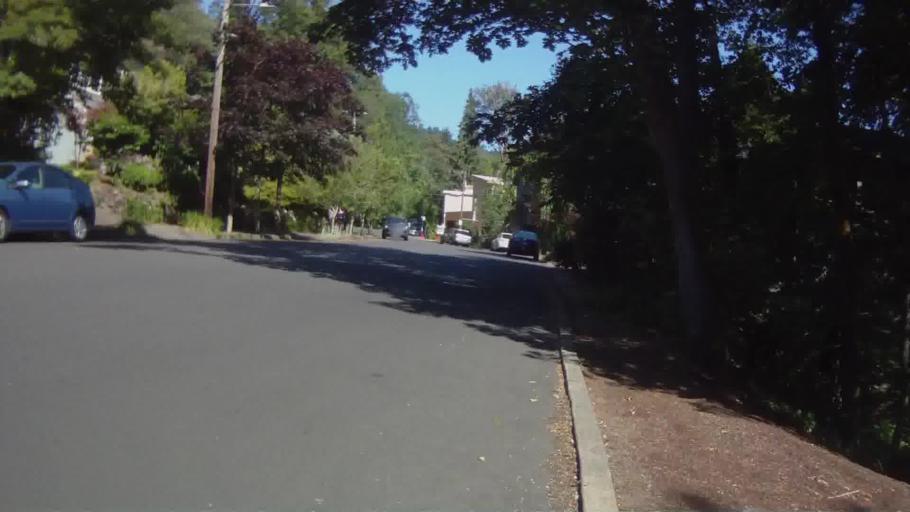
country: US
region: Oregon
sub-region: Multnomah County
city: Portland
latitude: 45.5379
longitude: -122.7187
